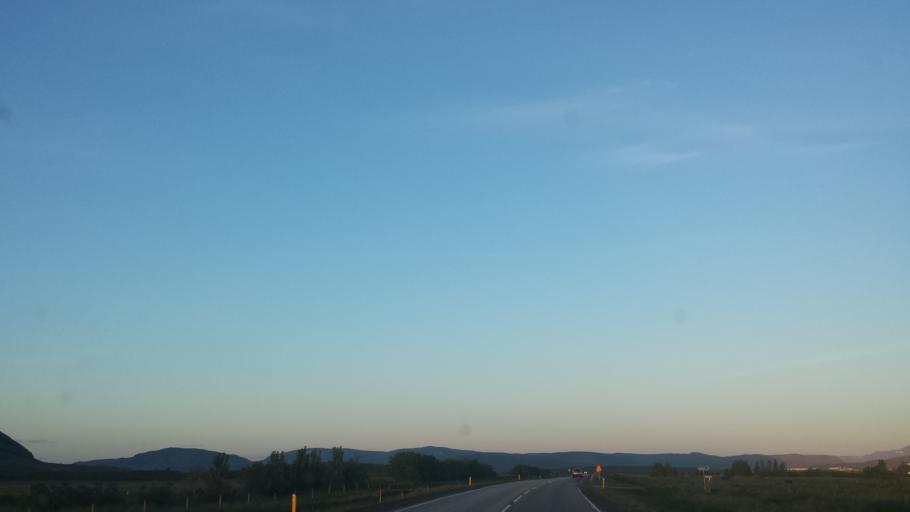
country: IS
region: Capital Region
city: Mosfellsbaer
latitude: 64.2124
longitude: -21.7729
